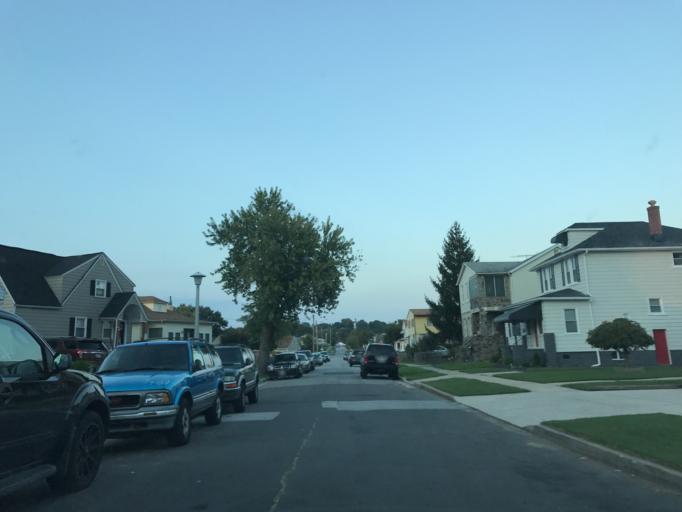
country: US
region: Maryland
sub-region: Baltimore County
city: Dundalk
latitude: 39.2758
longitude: -76.5302
